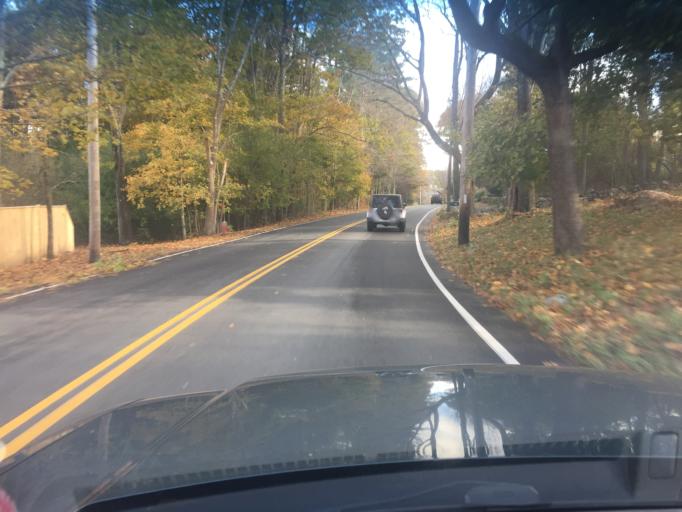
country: US
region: Massachusetts
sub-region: Norfolk County
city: Medfield
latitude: 42.2114
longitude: -71.3111
